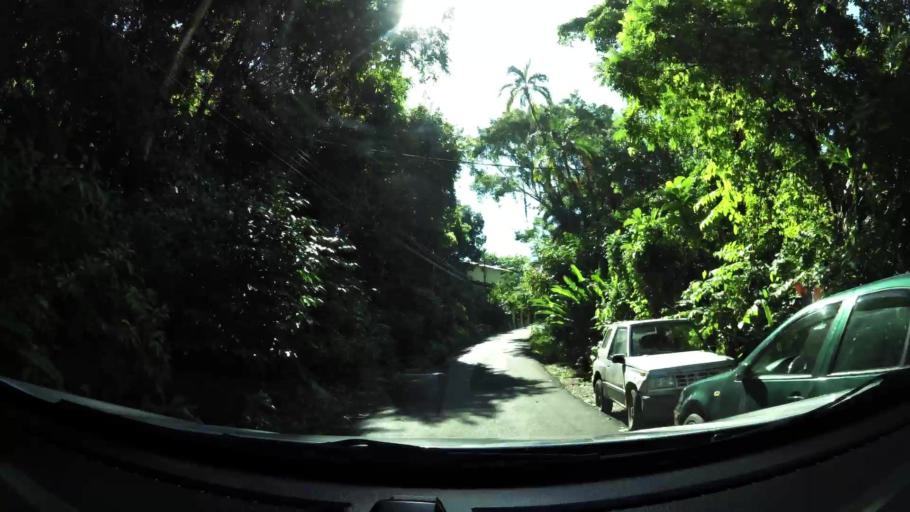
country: CR
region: Puntarenas
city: Quepos
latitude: 9.3980
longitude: -84.1677
